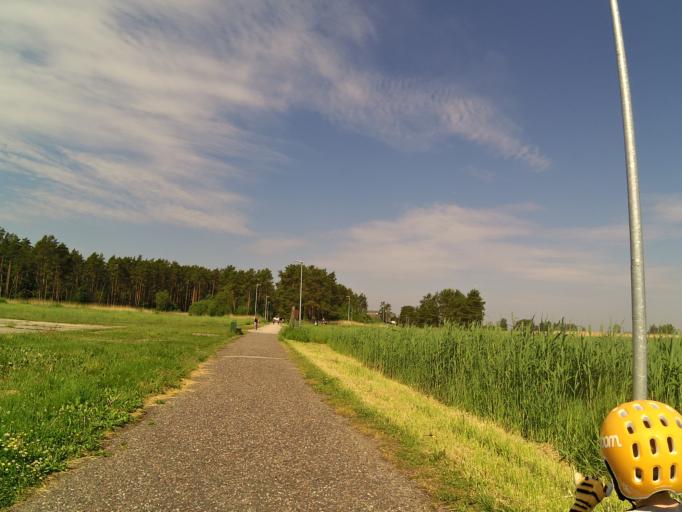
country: EE
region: Laeaene
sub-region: Haapsalu linn
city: Haapsalu
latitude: 58.9392
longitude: 23.5232
